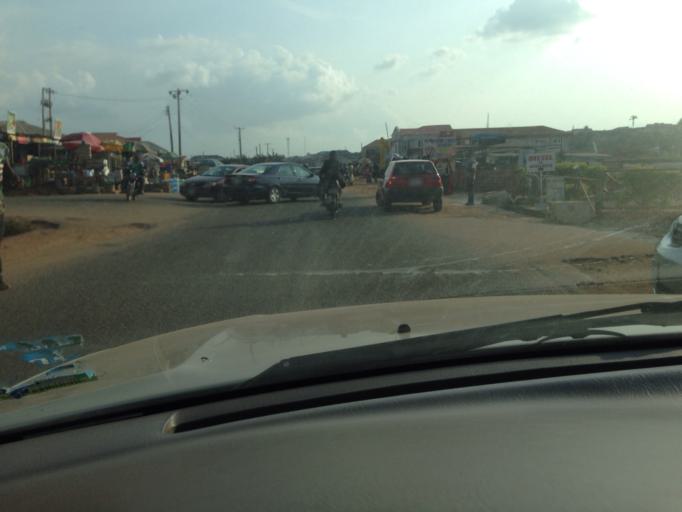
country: NG
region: Oyo
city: Ibadan
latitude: 7.4369
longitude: 3.9471
